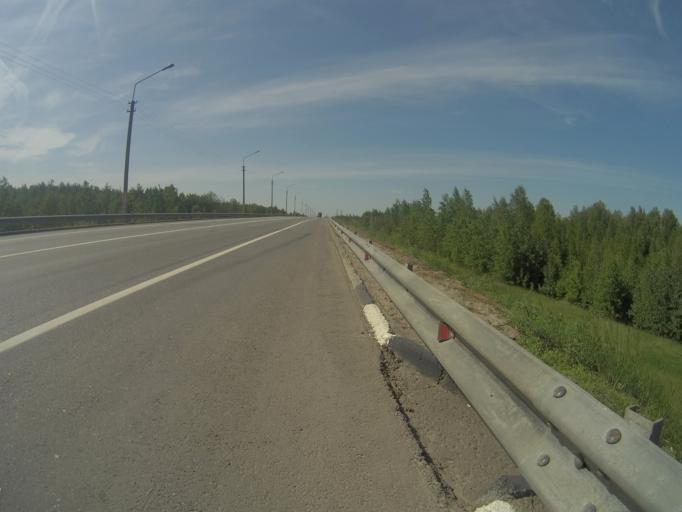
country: RU
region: Vladimir
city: Vorsha
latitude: 56.0745
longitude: 40.2164
